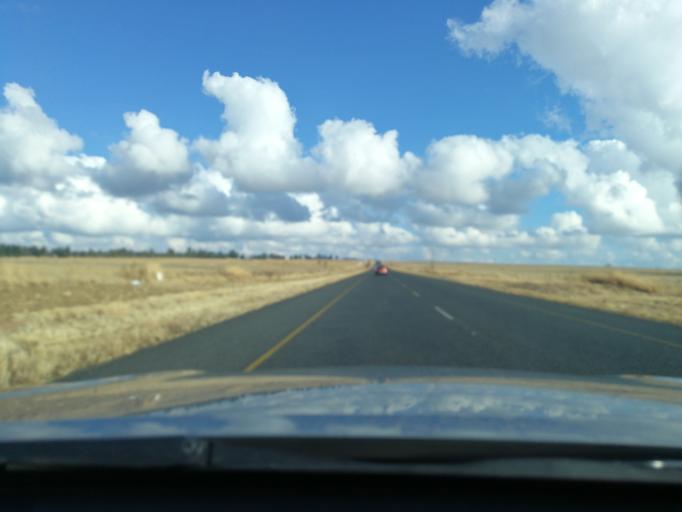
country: ZA
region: Orange Free State
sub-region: Thabo Mofutsanyana District Municipality
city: Bethlehem
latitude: -28.1055
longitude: 28.3501
